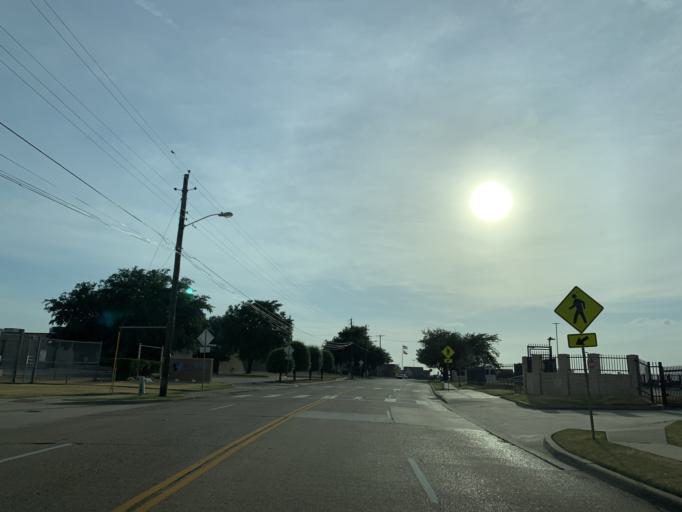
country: US
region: Texas
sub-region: Dallas County
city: Cockrell Hill
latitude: 32.6941
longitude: -96.8969
